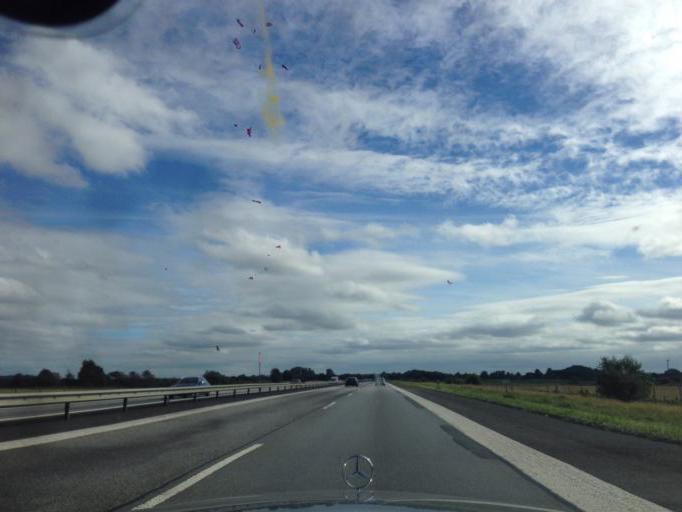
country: DE
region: Schleswig-Holstein
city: Lottorf
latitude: 54.4392
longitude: 9.5913
